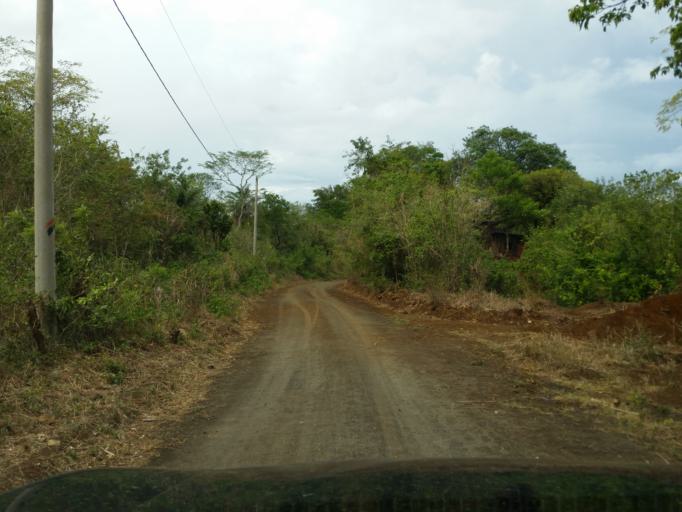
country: NI
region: Managua
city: El Crucero
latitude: 11.9844
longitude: -86.3868
